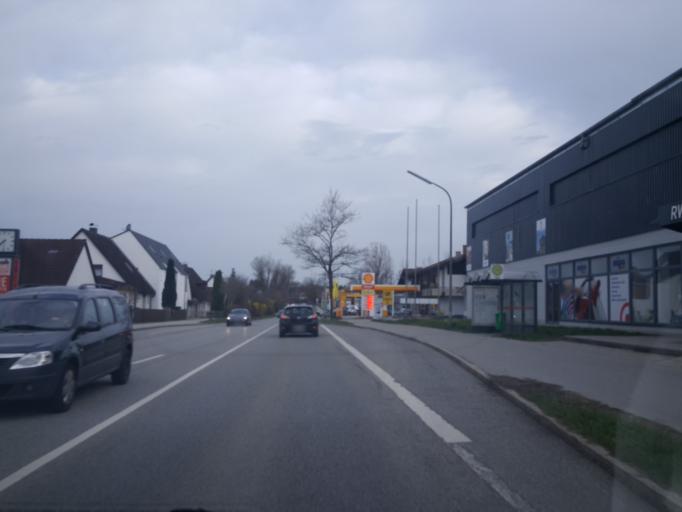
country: DE
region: Bavaria
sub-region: Upper Bavaria
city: Penzberg
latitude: 47.7638
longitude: 11.3639
